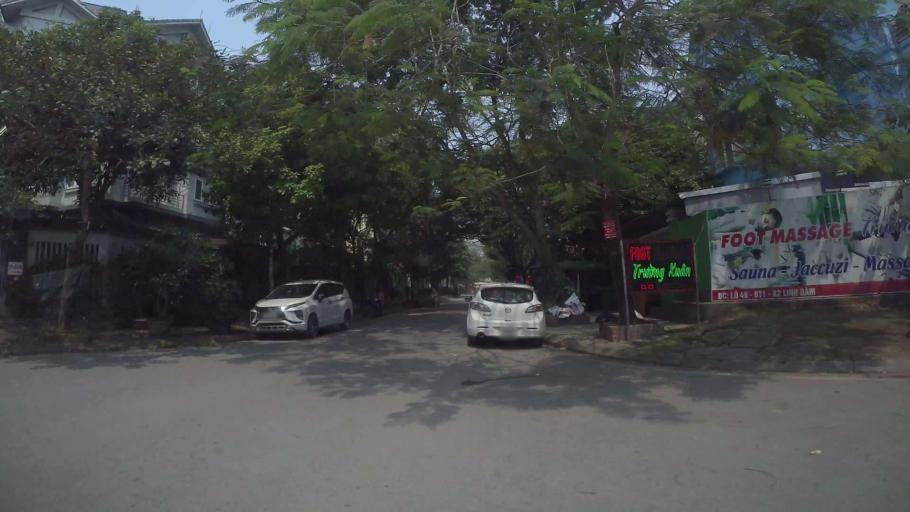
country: VN
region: Ha Noi
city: Van Dien
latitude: 20.9678
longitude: 105.8256
